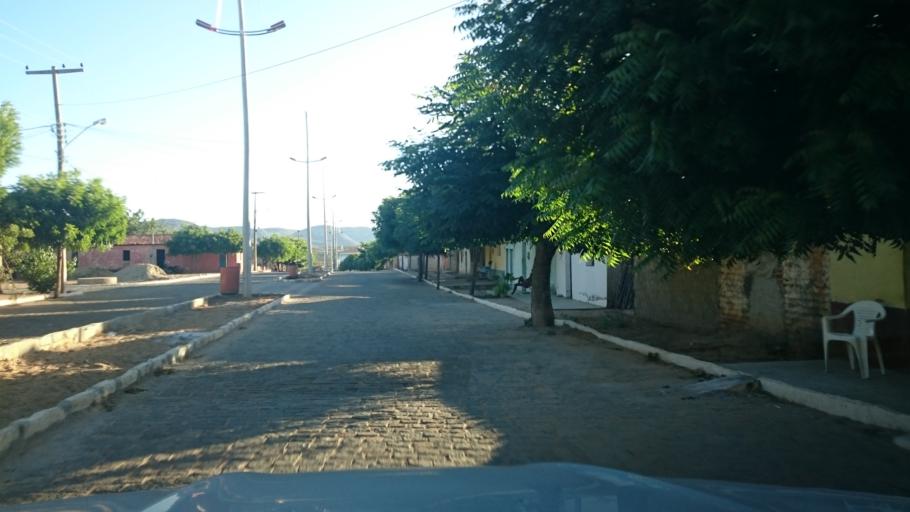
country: BR
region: Rio Grande do Norte
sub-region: Umarizal
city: Umarizal
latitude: -5.9347
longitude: -37.9375
